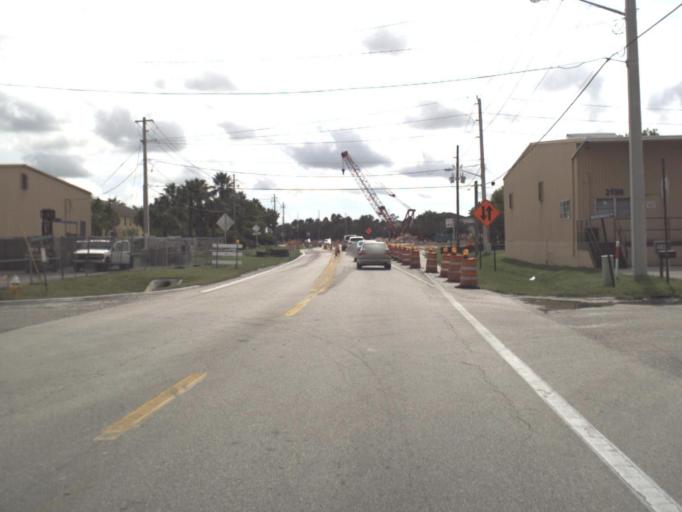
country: US
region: Florida
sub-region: Lee County
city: Fort Myers
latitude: 26.6129
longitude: -81.8518
